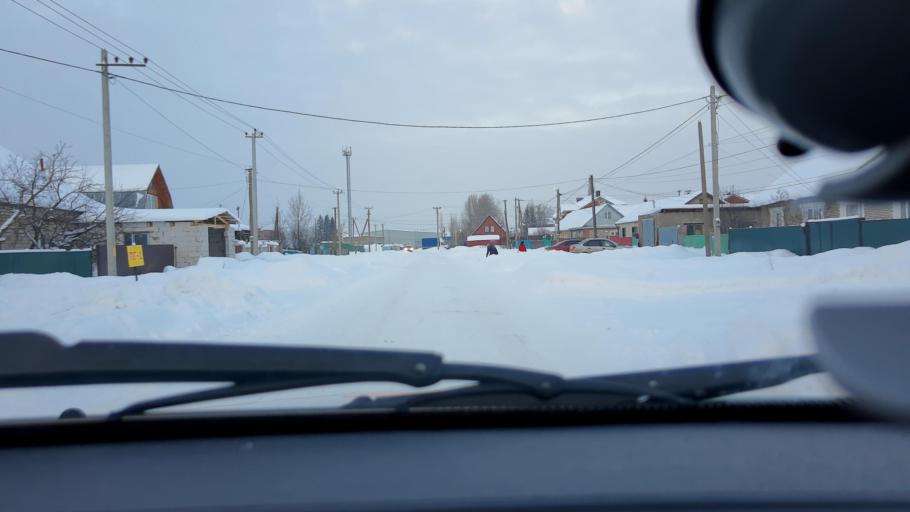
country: RU
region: Bashkortostan
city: Ufa
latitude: 54.6136
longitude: 55.8984
